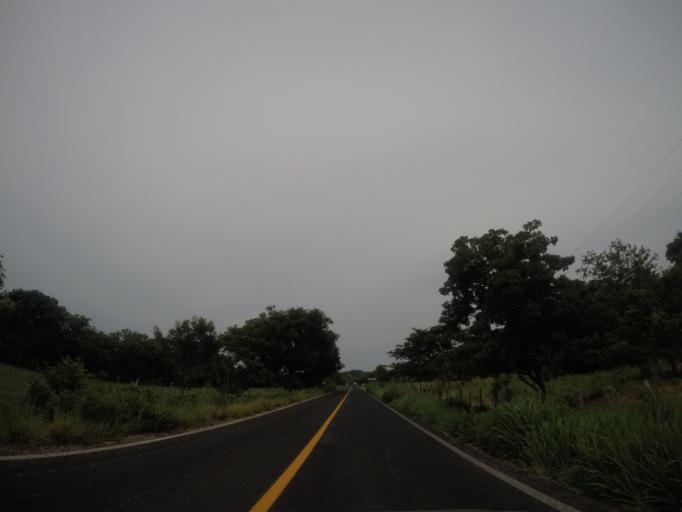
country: MX
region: Oaxaca
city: San Pedro Mixtepec
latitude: 15.9506
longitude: -97.2642
